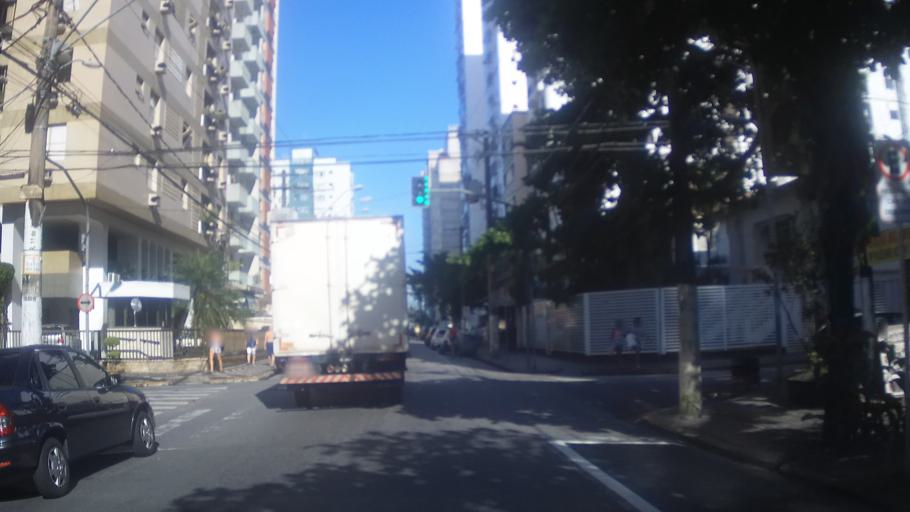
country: BR
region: Sao Paulo
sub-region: Sao Vicente
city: Sao Vicente
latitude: -23.9717
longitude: -46.3724
